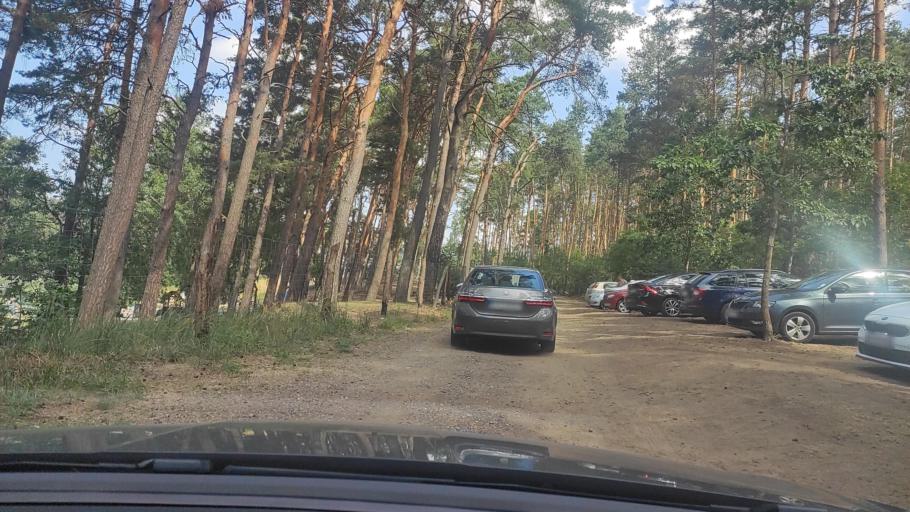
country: PL
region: Greater Poland Voivodeship
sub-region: Powiat gnieznienski
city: Kiszkowo
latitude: 52.5169
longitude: 17.1779
